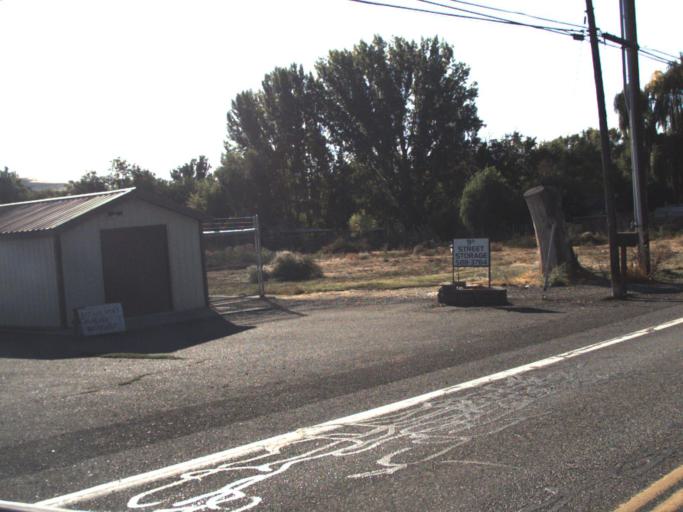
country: US
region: Washington
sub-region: Benton County
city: Benton City
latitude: 46.2615
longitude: -119.4874
